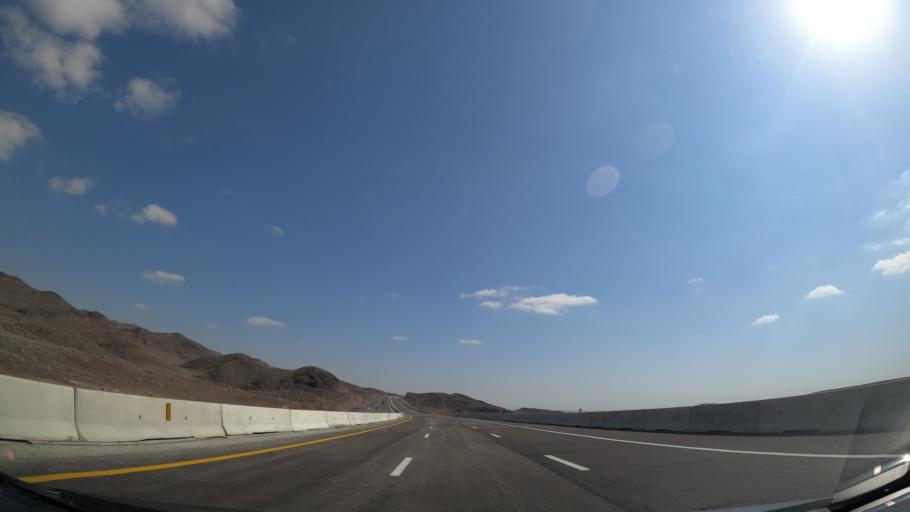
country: IR
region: Alborz
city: Eshtehard
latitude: 35.6640
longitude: 50.6502
